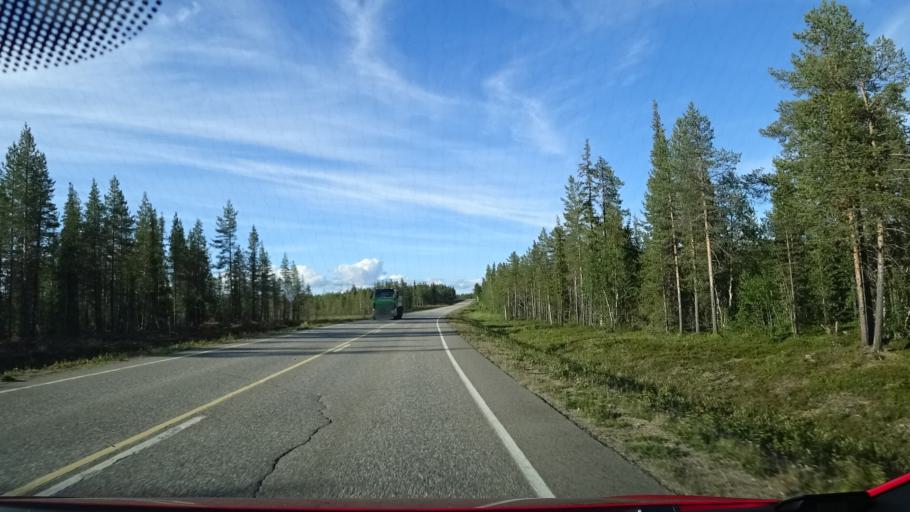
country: FI
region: Lapland
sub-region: Pohjois-Lappi
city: Sodankylae
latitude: 67.9260
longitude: 26.7539
